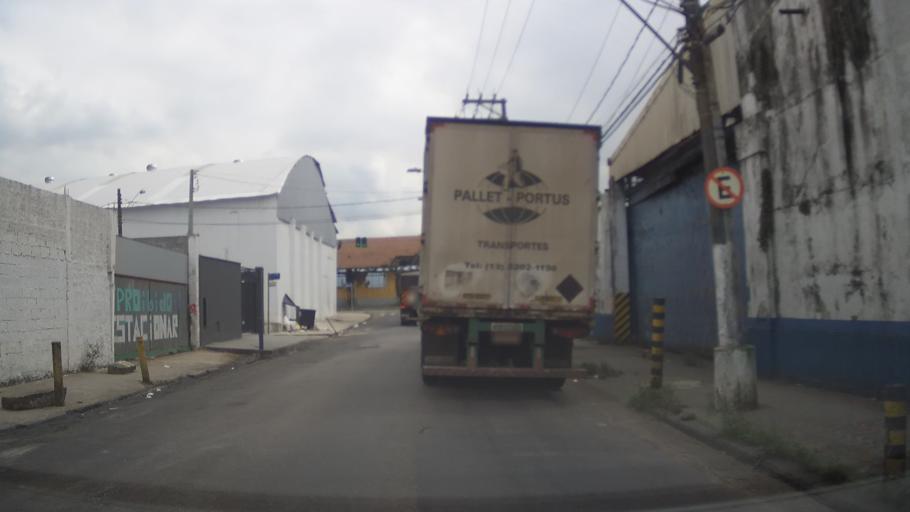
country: BR
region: Sao Paulo
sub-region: Santos
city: Santos
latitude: -23.9338
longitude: -46.3205
